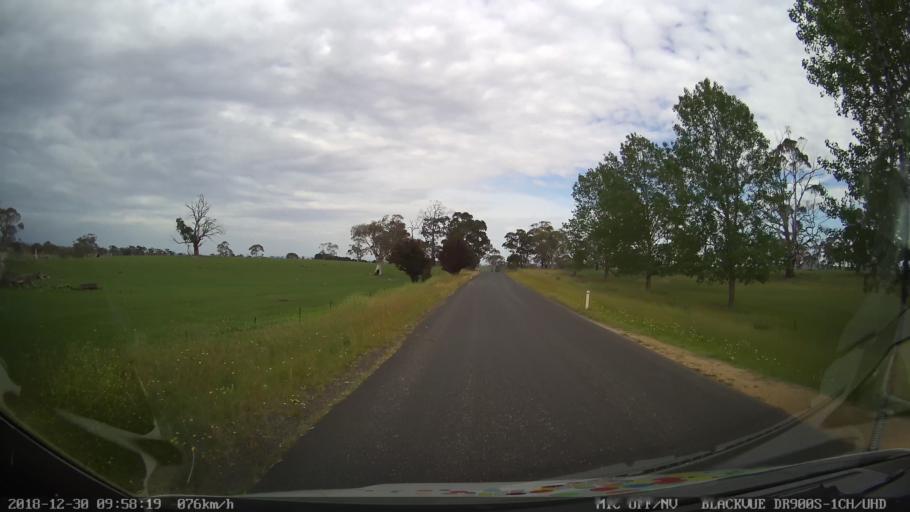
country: AU
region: New South Wales
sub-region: Cooma-Monaro
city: Cooma
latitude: -36.5225
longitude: 149.2278
